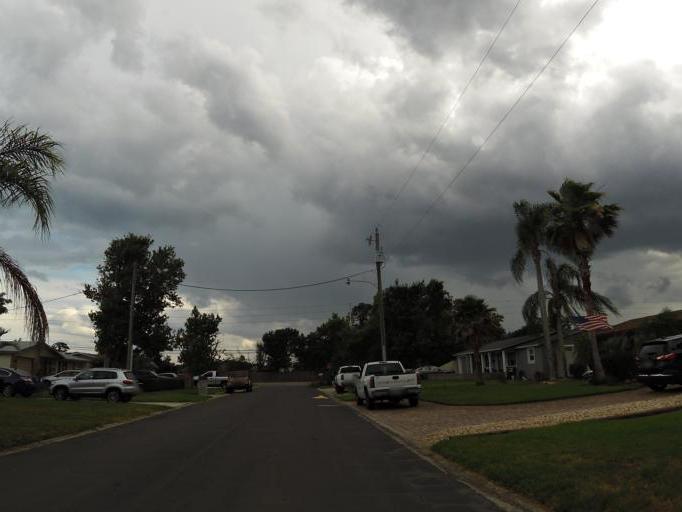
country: US
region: Florida
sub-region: Duval County
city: Jacksonville Beach
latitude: 30.2683
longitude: -81.3920
